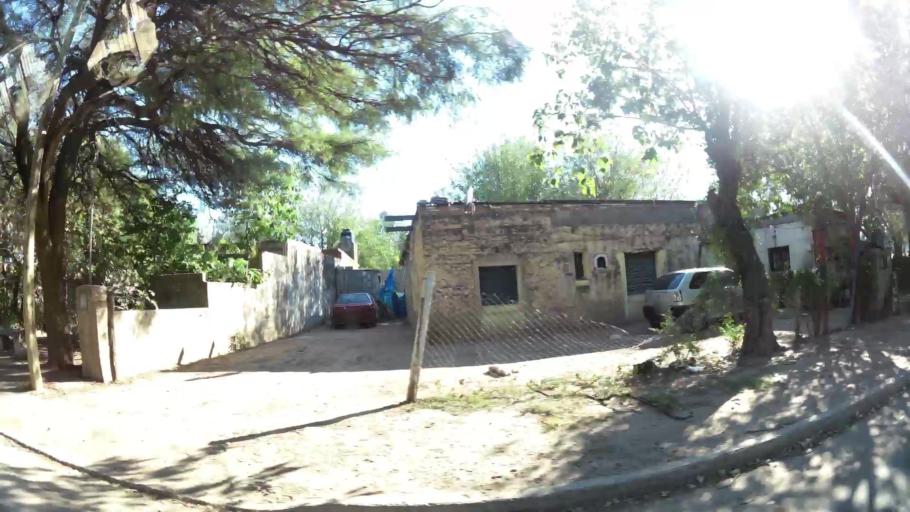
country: AR
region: Cordoba
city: Villa Allende
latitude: -31.3312
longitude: -64.2597
